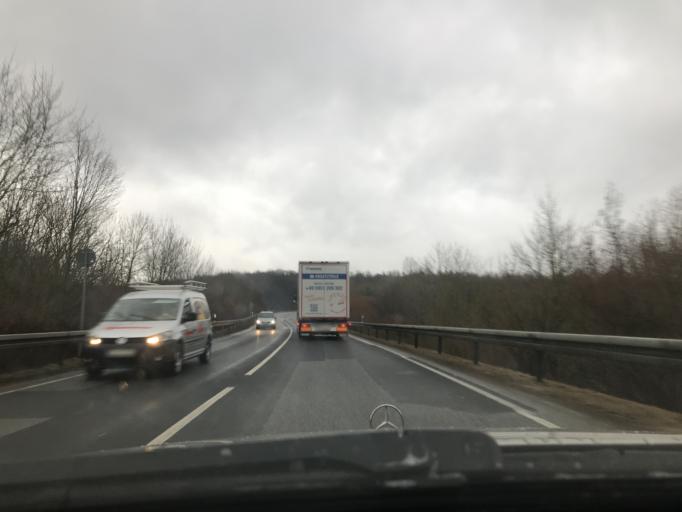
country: DE
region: Hesse
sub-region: Regierungsbezirk Kassel
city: Calden
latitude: 51.4007
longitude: 9.4240
